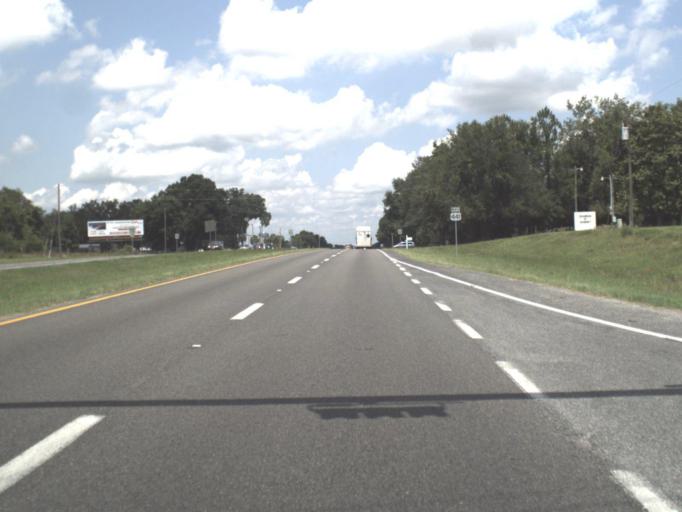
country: US
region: Florida
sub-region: Alachua County
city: High Springs
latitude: 29.8044
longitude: -82.5267
